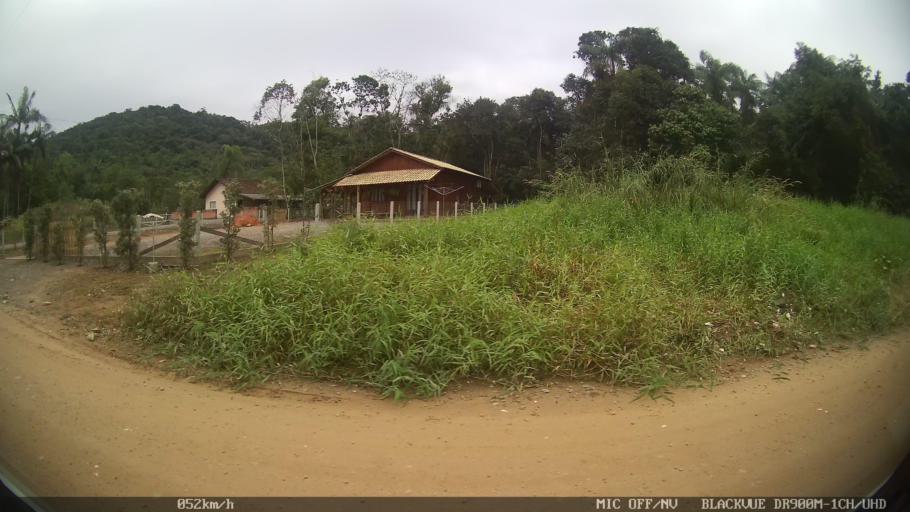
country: BR
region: Santa Catarina
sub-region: Joinville
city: Joinville
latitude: -26.2715
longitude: -48.9335
